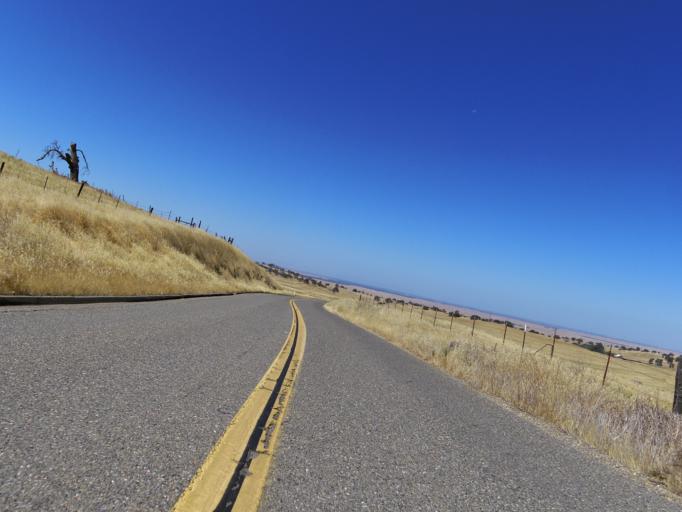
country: US
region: California
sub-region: Merced County
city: Planada
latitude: 37.5722
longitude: -120.3111
